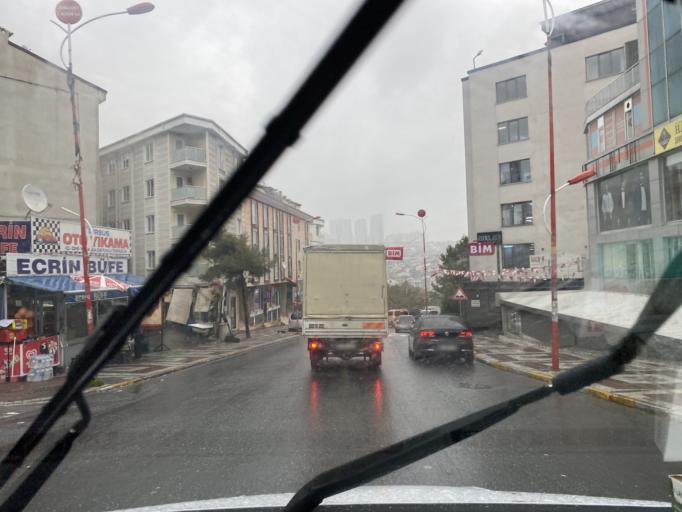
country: TR
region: Istanbul
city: Esenyurt
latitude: 41.0184
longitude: 28.6656
